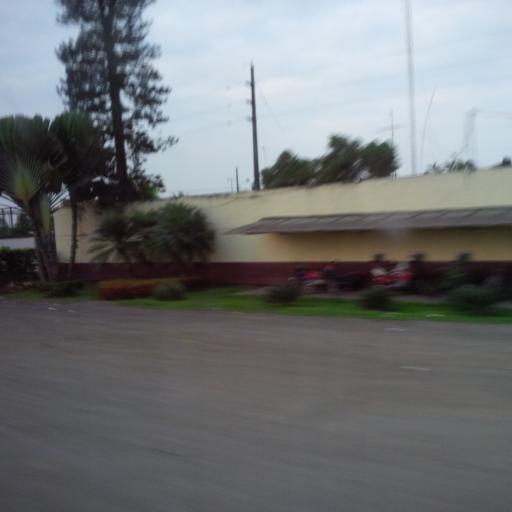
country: EC
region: Canar
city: La Troncal
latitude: -2.3385
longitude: -79.3884
